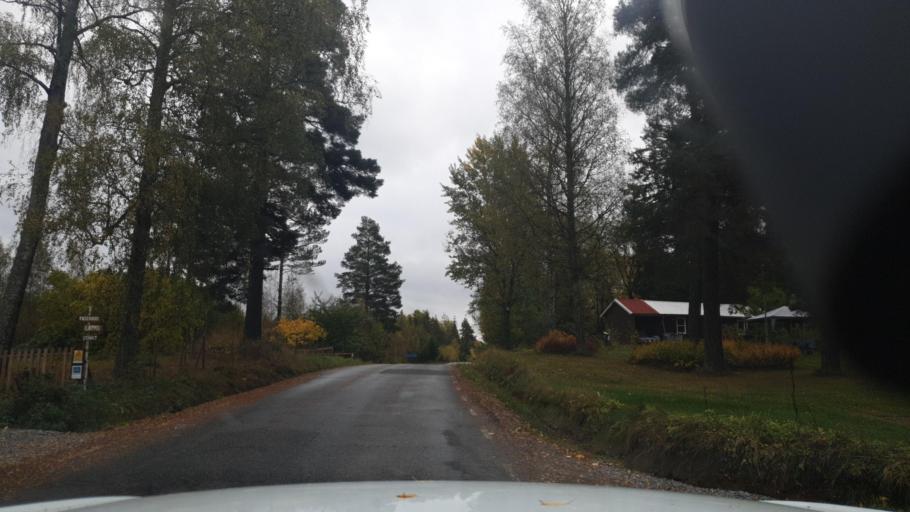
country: SE
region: Vaermland
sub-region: Karlstads Kommun
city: Valberg
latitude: 59.4189
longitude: 13.1151
